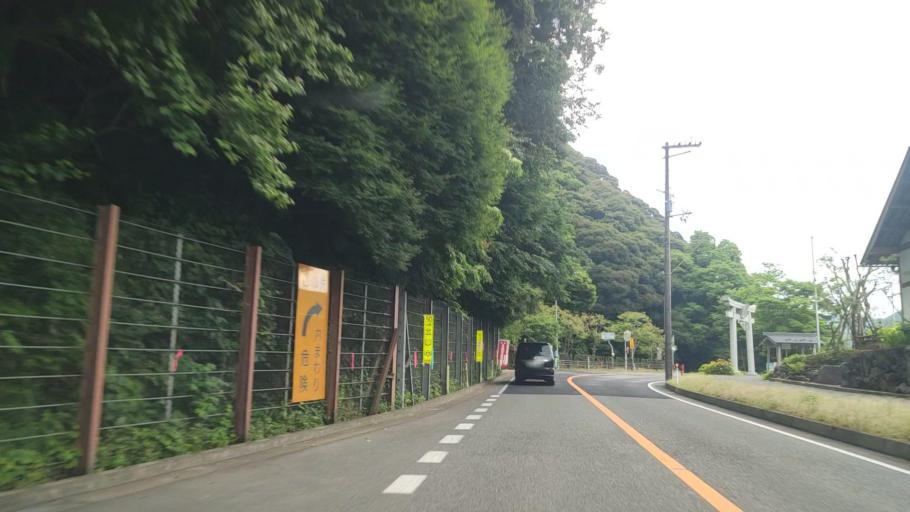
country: JP
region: Hyogo
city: Toyooka
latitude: 35.6412
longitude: 134.8288
